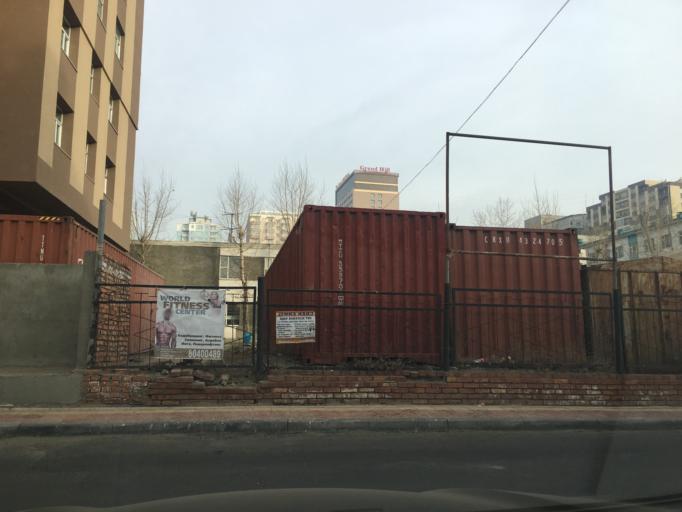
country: MN
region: Ulaanbaatar
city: Ulaanbaatar
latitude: 47.9155
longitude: 106.8829
